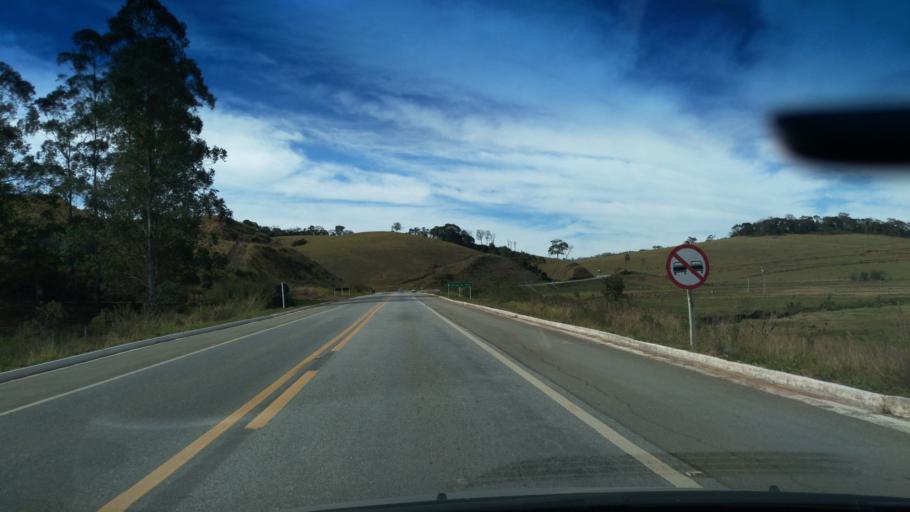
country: BR
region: Minas Gerais
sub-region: Borda Da Mata
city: Borda da Mata
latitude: -22.1512
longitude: -46.1268
